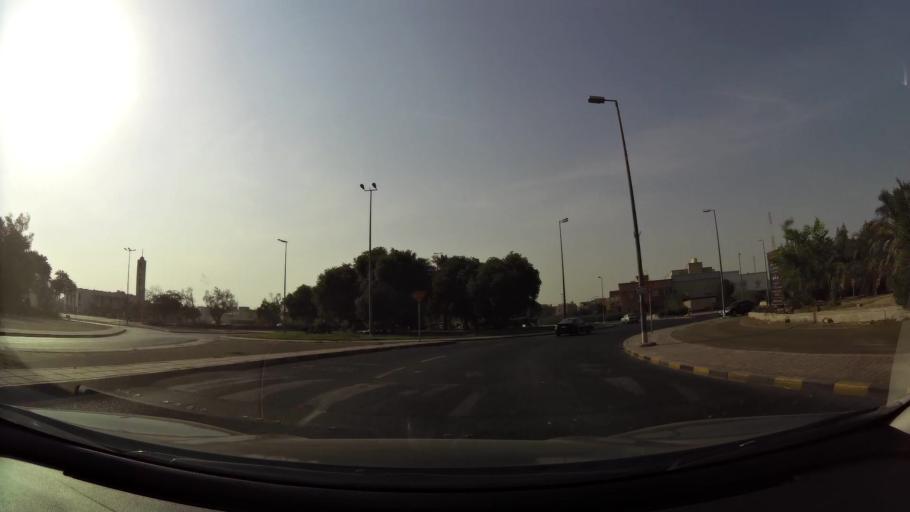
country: KW
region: Al Ahmadi
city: Ar Riqqah
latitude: 29.1658
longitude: 48.0821
